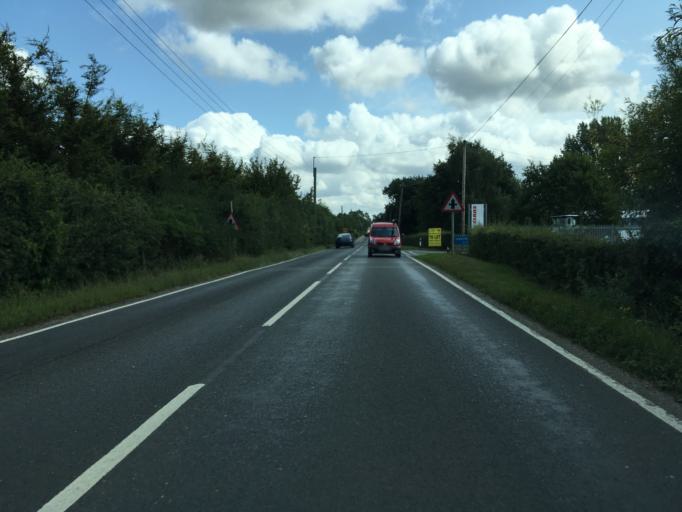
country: GB
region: England
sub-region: Kent
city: Headcorn
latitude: 51.1800
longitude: 0.6118
